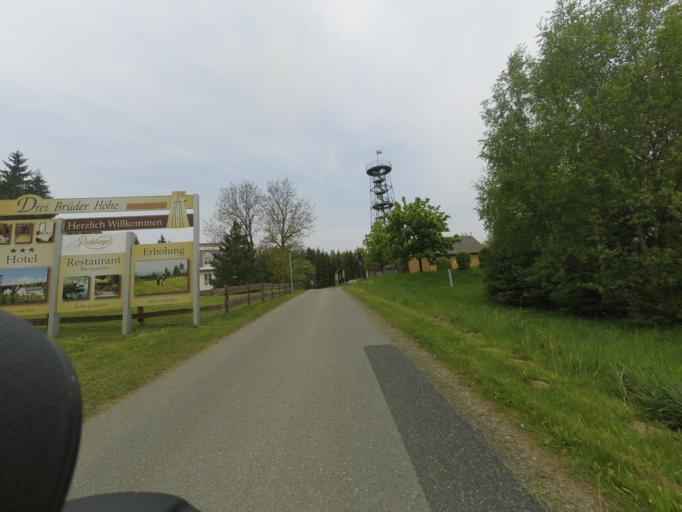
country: DE
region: Saxony
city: Grossruckerswalde
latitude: 50.6562
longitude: 13.1247
